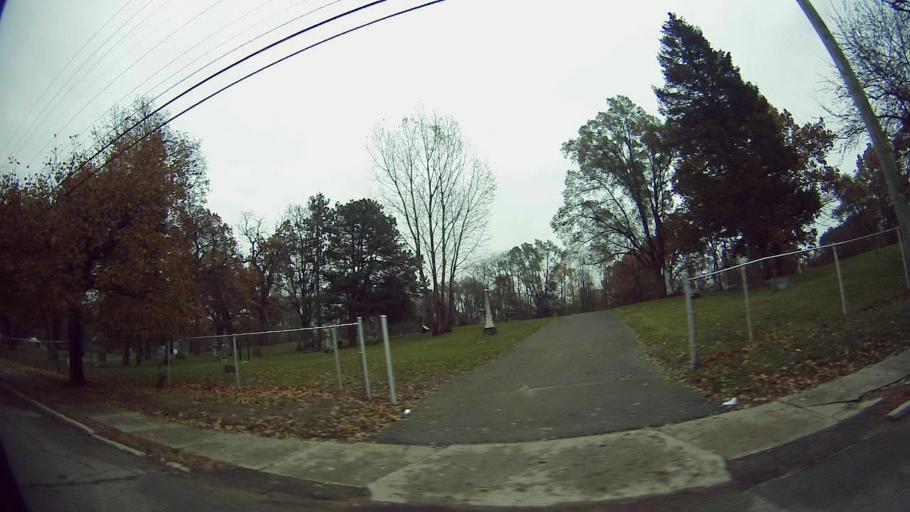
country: US
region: Michigan
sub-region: Wayne County
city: Redford
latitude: 42.4250
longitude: -83.2582
